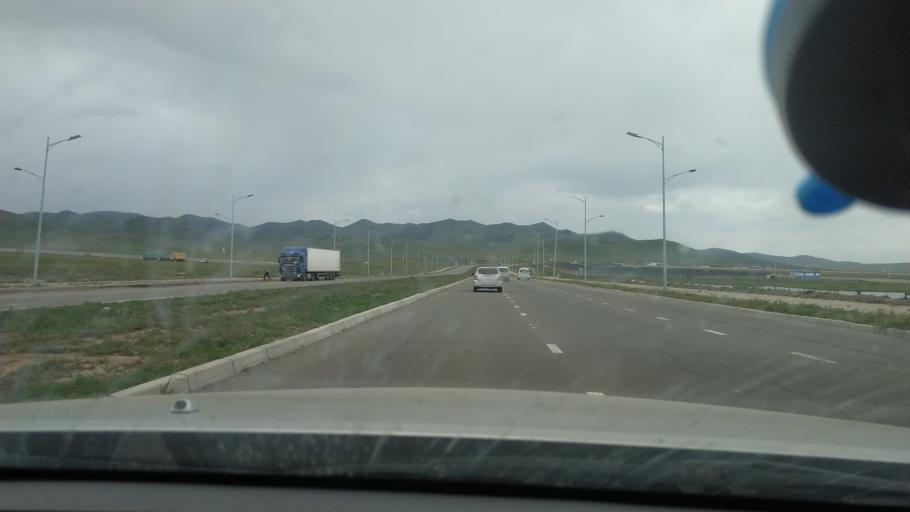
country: MN
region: Ulaanbaatar
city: Ulaanbaatar
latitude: 47.8353
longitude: 106.7881
